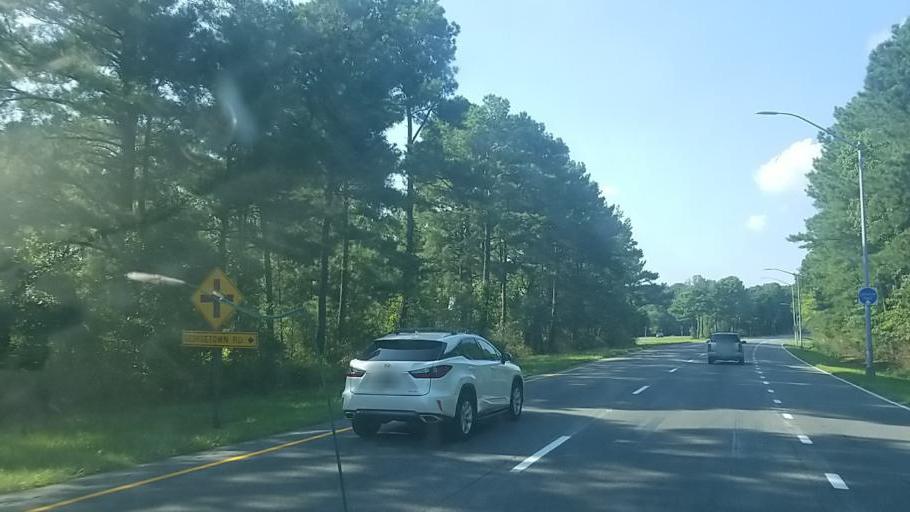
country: US
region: Maryland
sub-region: Worcester County
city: Berlin
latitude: 38.3471
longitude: -75.2144
